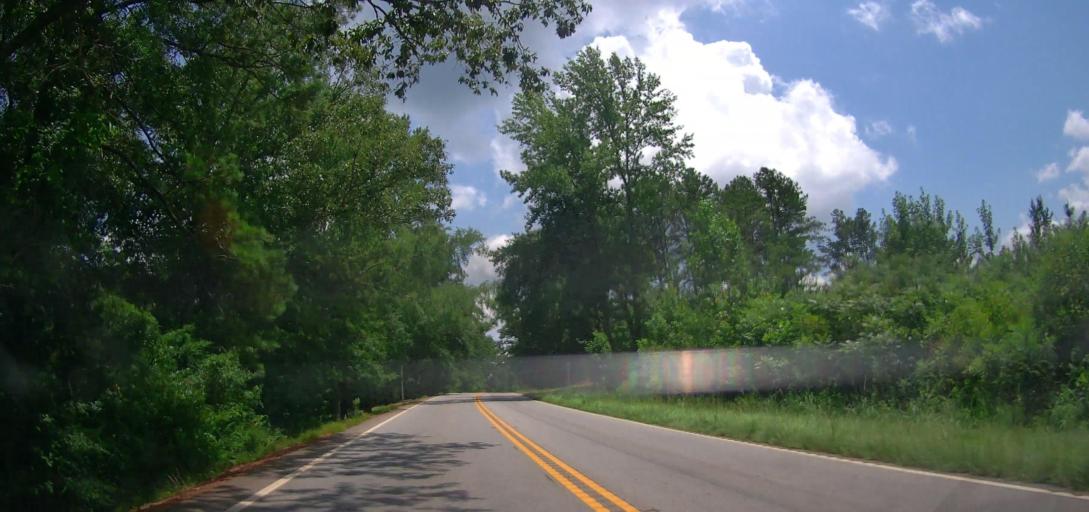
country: US
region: Georgia
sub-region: Meriwether County
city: Greenville
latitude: 33.0277
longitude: -84.6895
